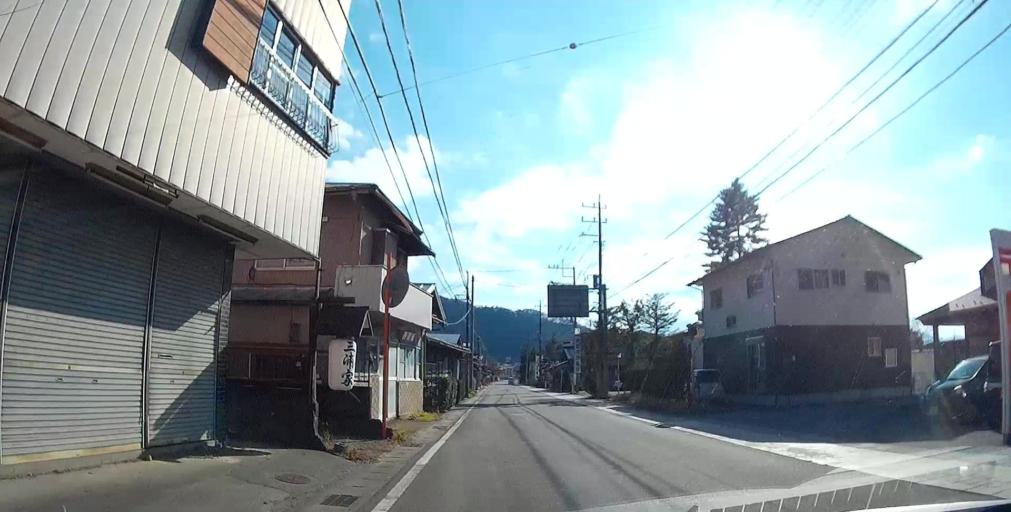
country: JP
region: Yamanashi
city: Fujikawaguchiko
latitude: 35.5292
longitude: 138.7733
